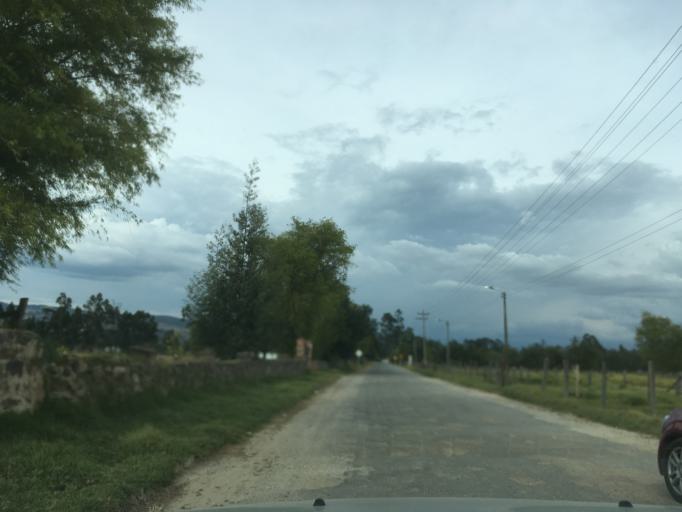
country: CO
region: Boyaca
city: Firavitoba
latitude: 5.6490
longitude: -72.9900
